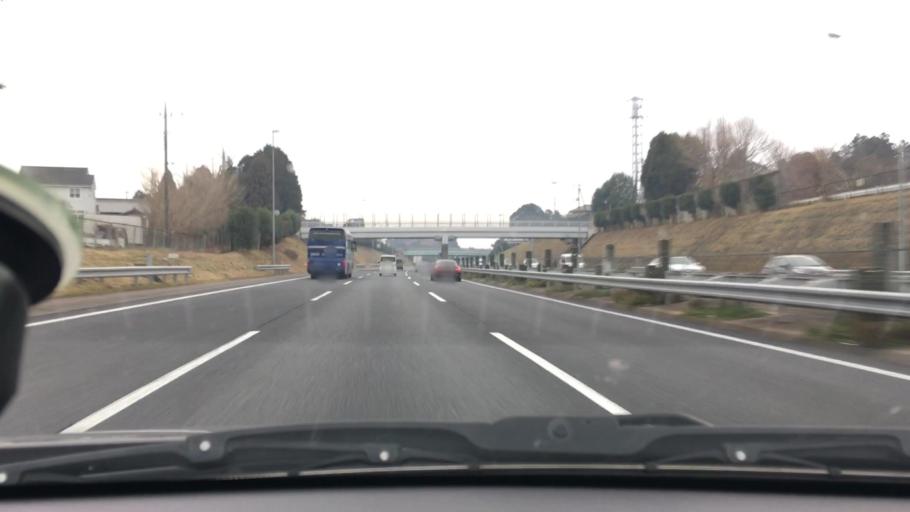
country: JP
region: Chiba
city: Shisui
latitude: 35.7312
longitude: 140.2961
